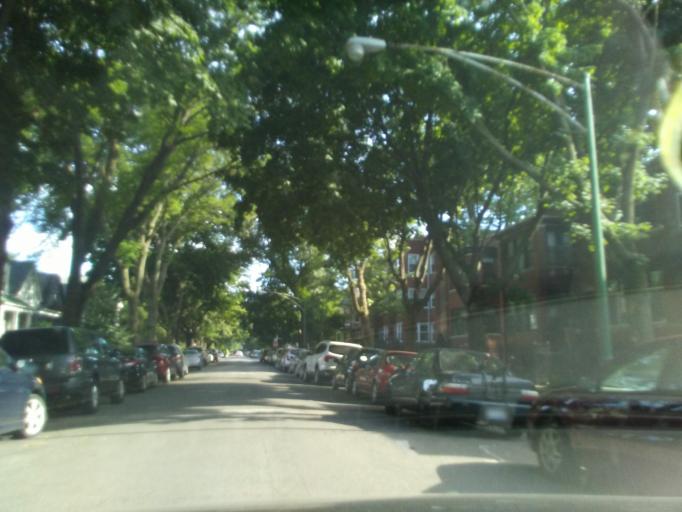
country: US
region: Illinois
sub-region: Cook County
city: Lincolnwood
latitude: 41.9758
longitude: -87.6764
